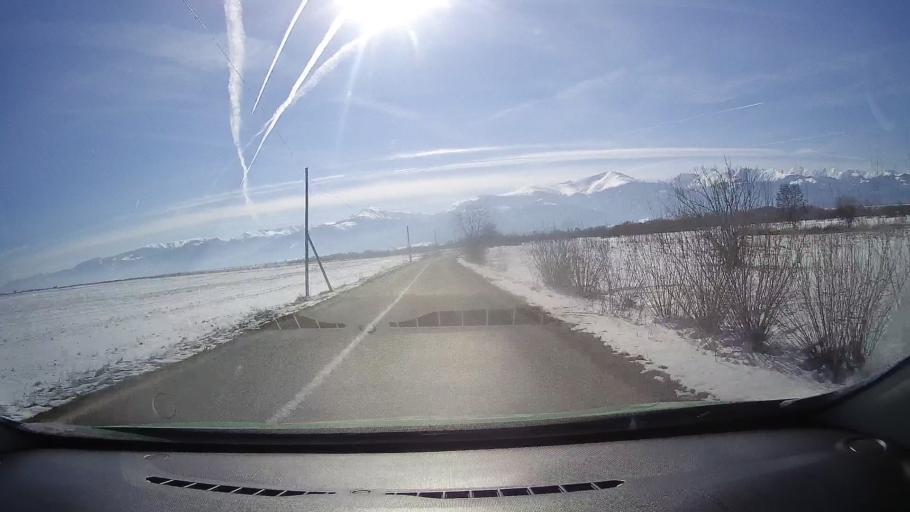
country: RO
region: Brasov
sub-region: Comuna Sambata de Sus
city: Sambata de Sus
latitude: 45.7445
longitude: 24.8431
